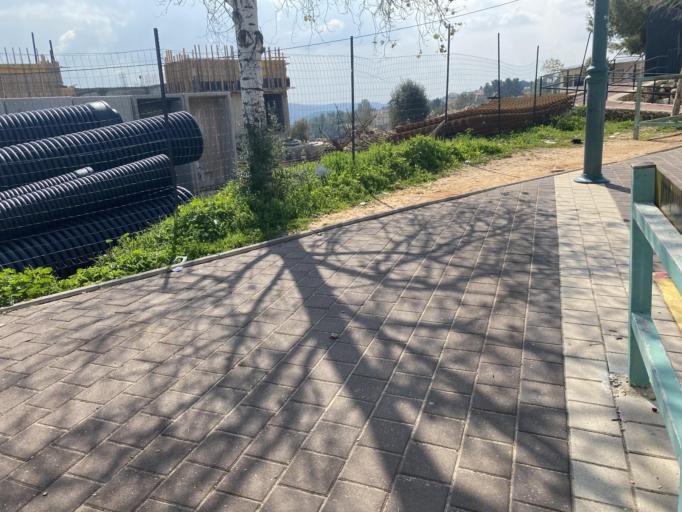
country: PS
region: West Bank
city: Karney Shomron
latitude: 32.1741
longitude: 35.0916
